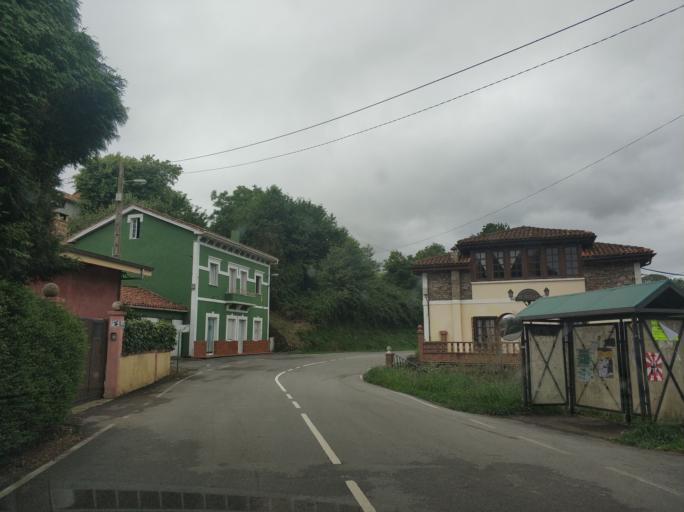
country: ES
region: Asturias
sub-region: Province of Asturias
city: Cudillero
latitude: 43.5468
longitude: -6.2178
